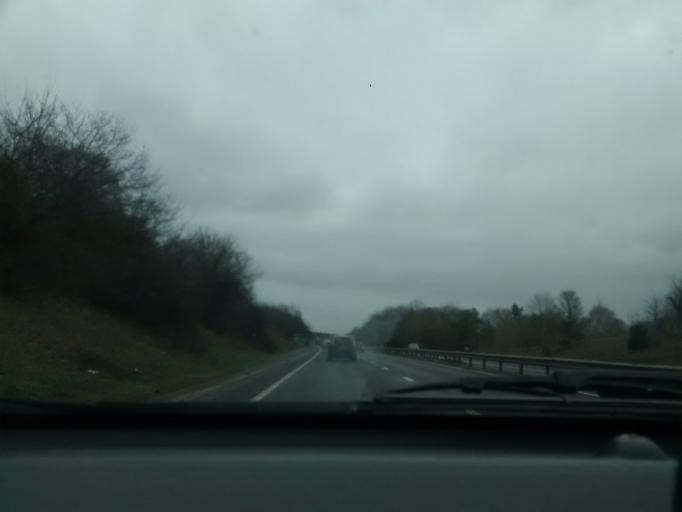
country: GB
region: England
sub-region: Suffolk
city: Needham Market
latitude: 52.1523
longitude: 1.0708
